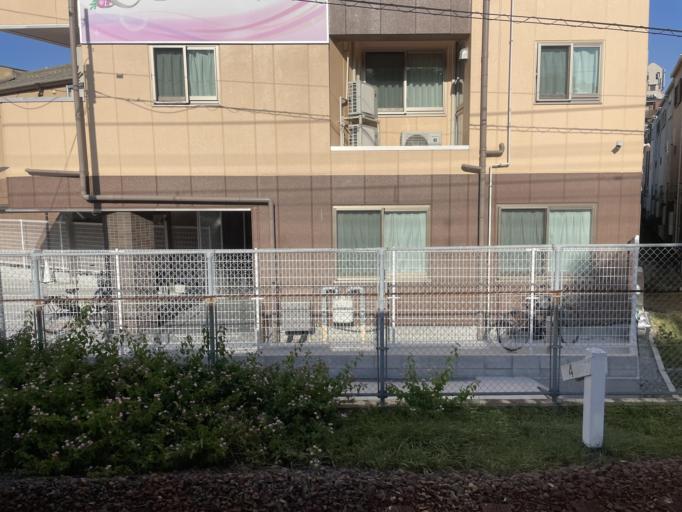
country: JP
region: Osaka
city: Osaka-shi
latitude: 34.6460
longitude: 135.4841
